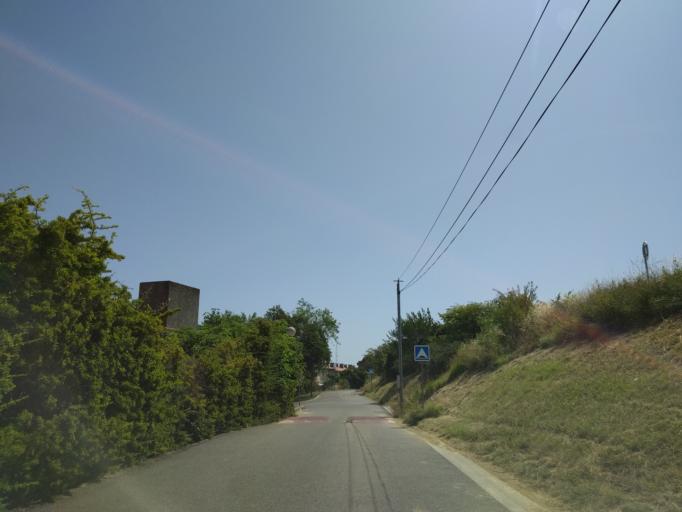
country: FR
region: Languedoc-Roussillon
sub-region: Departement de l'Aude
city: Carcassonne
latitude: 43.2057
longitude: 2.3748
